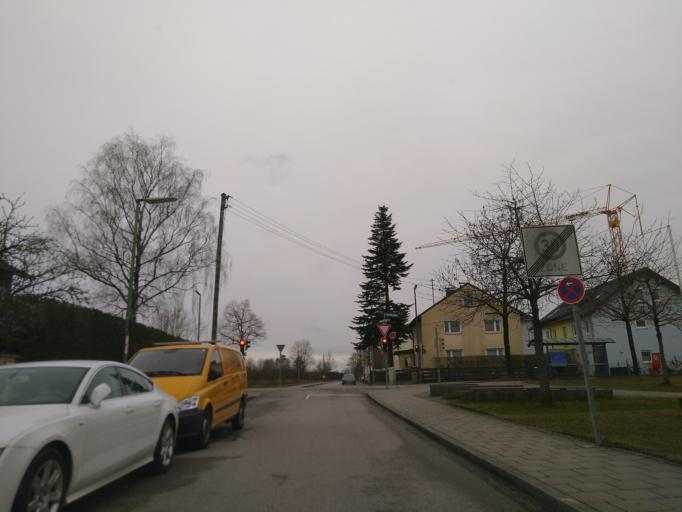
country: DE
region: Bavaria
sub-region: Upper Bavaria
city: Haar
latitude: 48.1293
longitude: 11.6760
